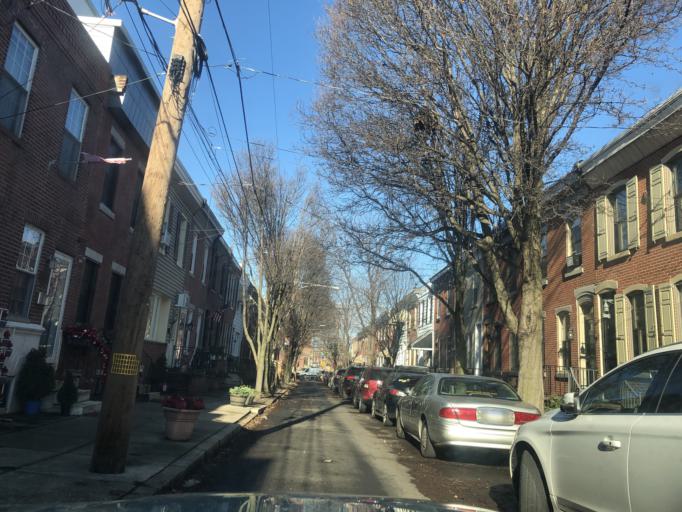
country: US
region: Pennsylvania
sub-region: Philadelphia County
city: Philadelphia
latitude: 39.9316
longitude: -75.1634
